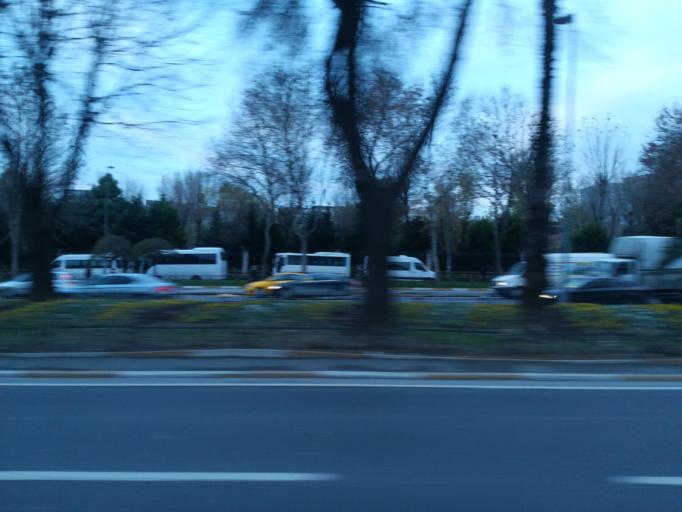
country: TR
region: Istanbul
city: Istanbul
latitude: 41.0184
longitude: 28.9384
